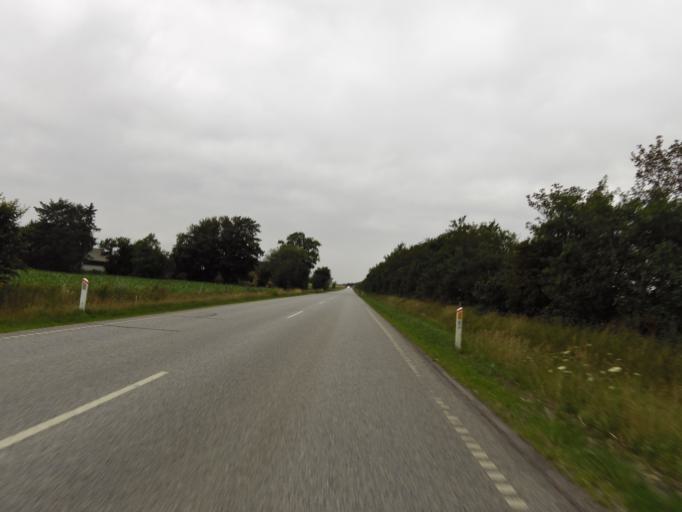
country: DK
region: South Denmark
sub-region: Haderslev Kommune
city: Gram
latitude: 55.2225
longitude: 8.9623
